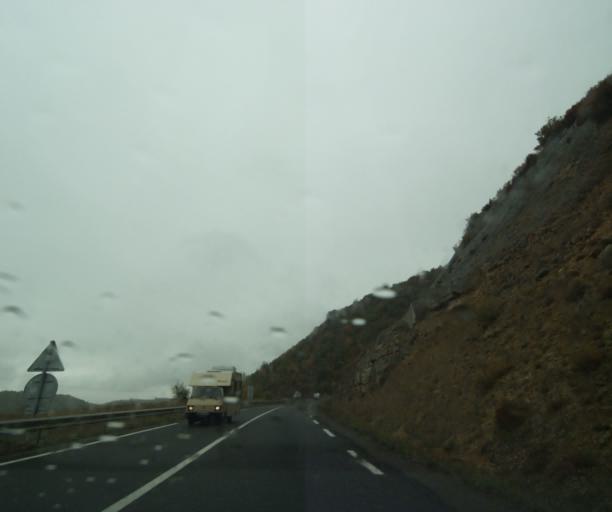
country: FR
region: Midi-Pyrenees
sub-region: Departement de l'Aveyron
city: Millau
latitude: 44.0946
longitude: 3.1242
